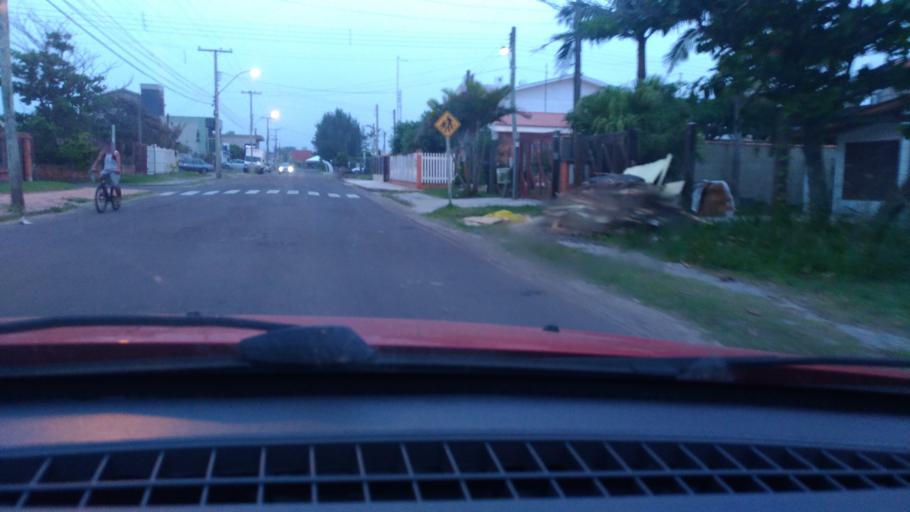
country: BR
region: Rio Grande do Sul
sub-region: Capao Da Canoa
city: Capao da Canoa
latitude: -29.8487
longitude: -50.0637
